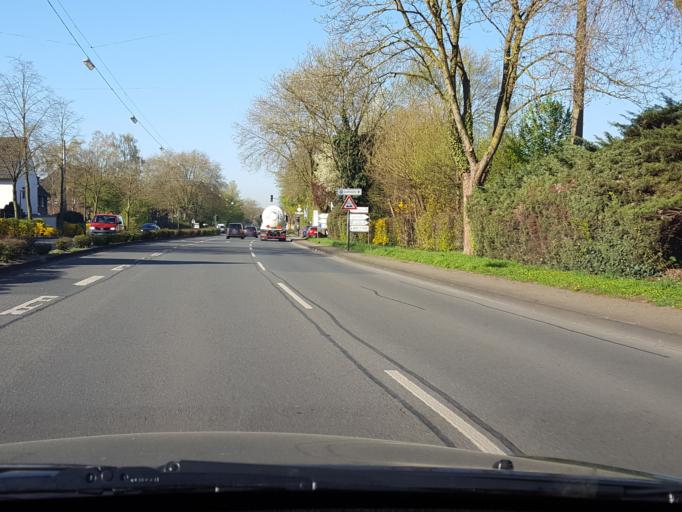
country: DE
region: North Rhine-Westphalia
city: Datteln
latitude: 51.6535
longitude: 7.3503
